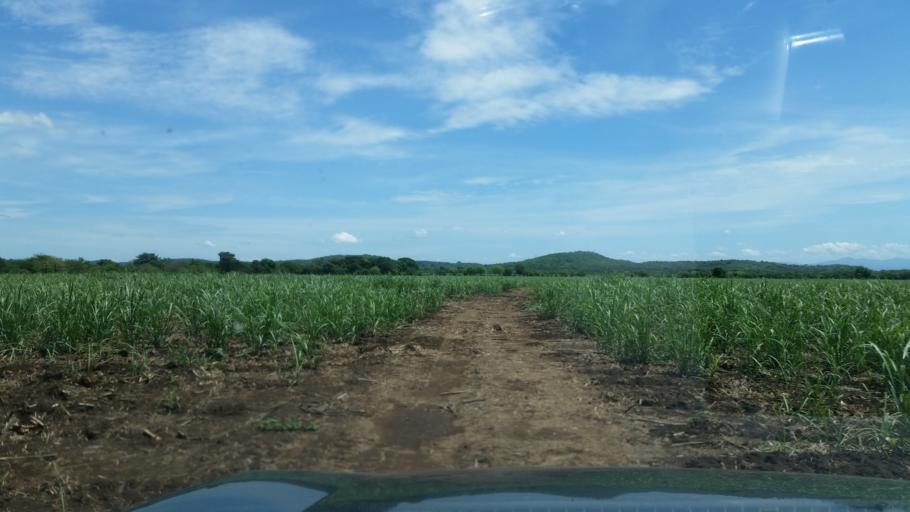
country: NI
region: Chinandega
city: Puerto Morazan
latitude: 12.7678
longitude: -87.1214
